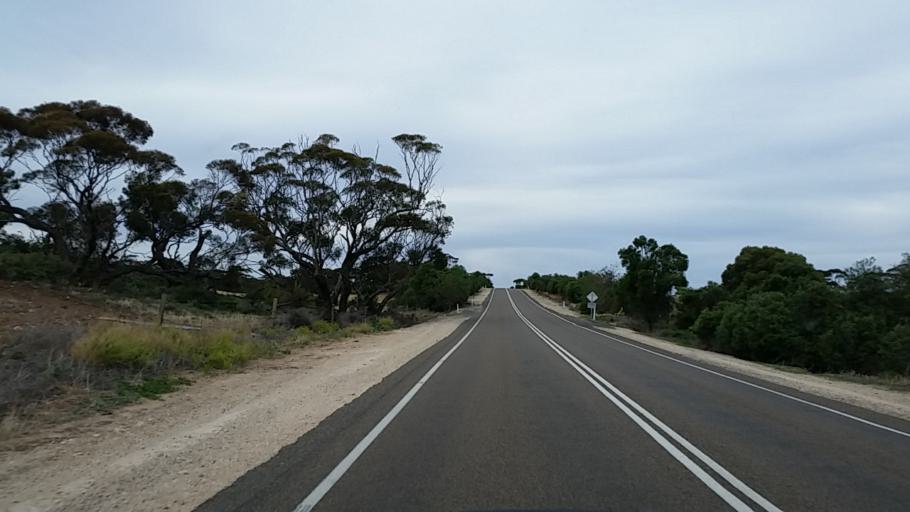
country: AU
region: South Australia
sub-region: Mid Murray
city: Mannum
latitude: -34.9316
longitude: 139.2418
